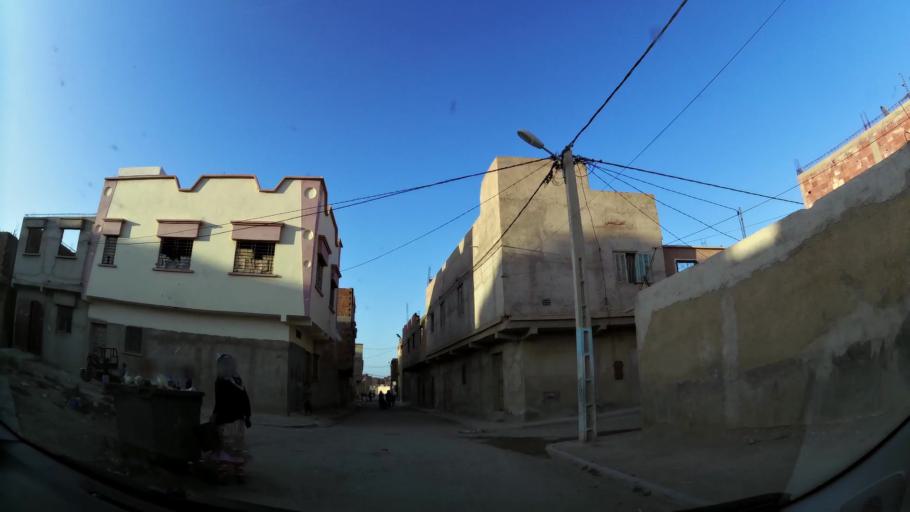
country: MA
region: Oriental
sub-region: Oujda-Angad
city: Oujda
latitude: 34.7113
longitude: -1.9065
